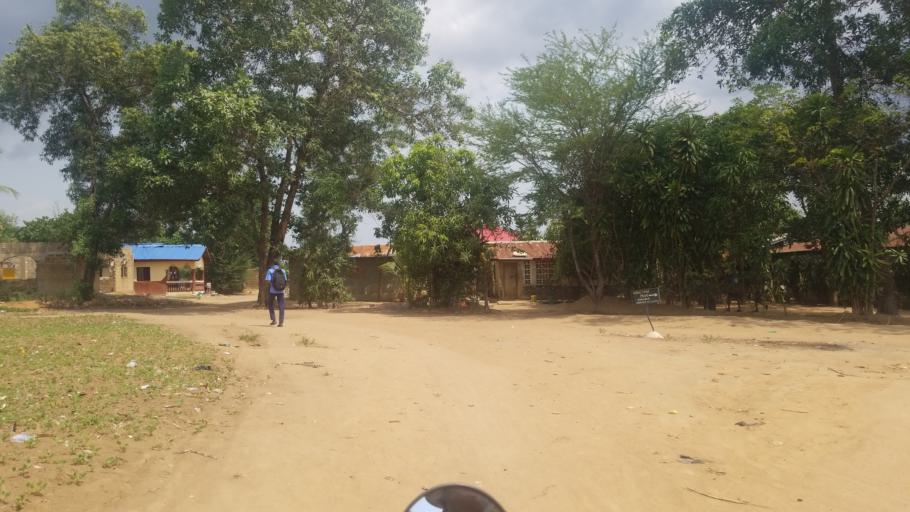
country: SL
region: Western Area
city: Waterloo
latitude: 8.3185
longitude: -13.0467
